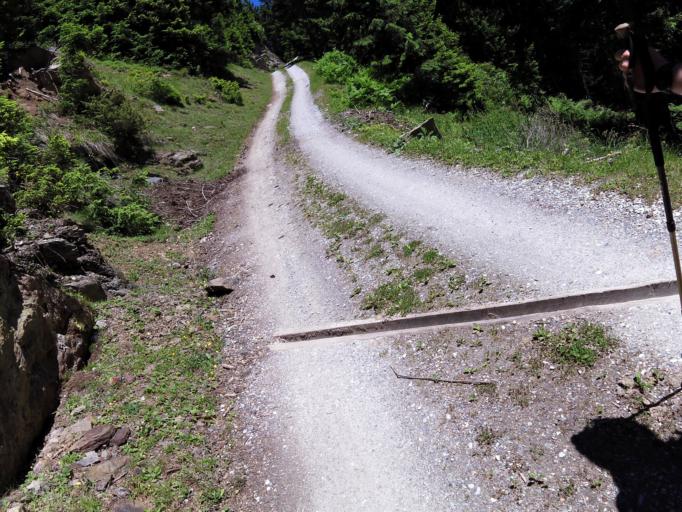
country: AT
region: Tyrol
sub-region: Politischer Bezirk Innsbruck Land
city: Neustift im Stubaital
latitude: 47.1131
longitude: 11.2911
